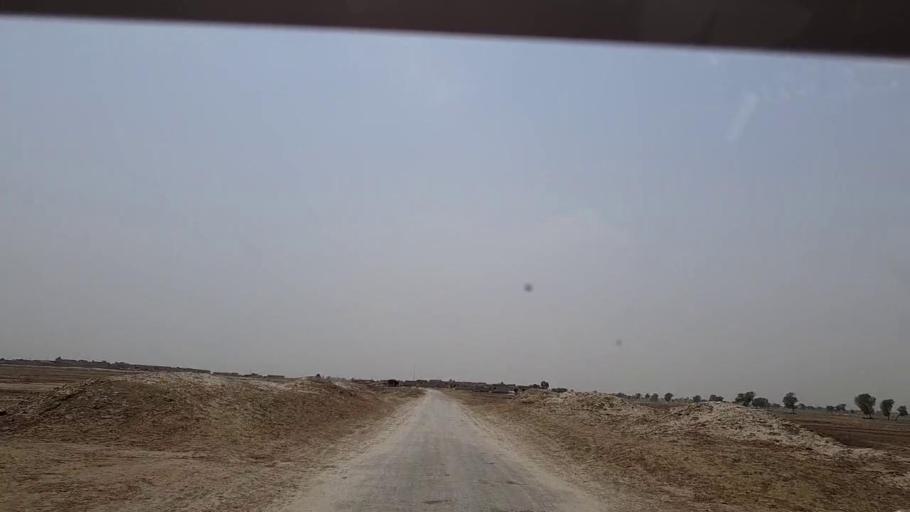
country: PK
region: Sindh
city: Khairpur Nathan Shah
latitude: 27.0174
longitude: 67.6100
